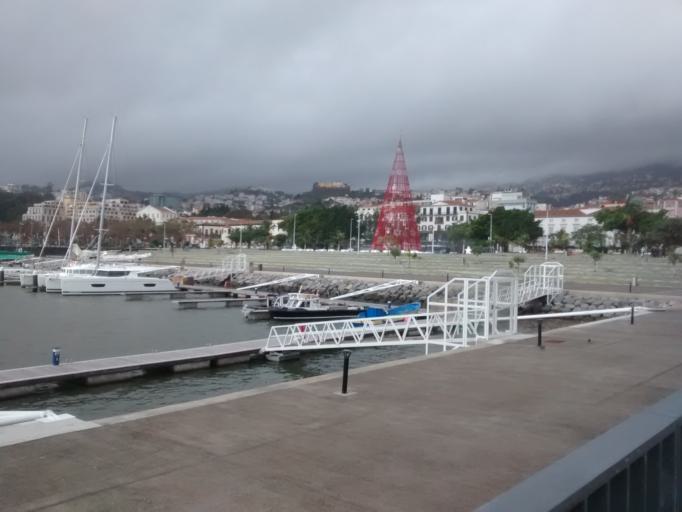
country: PT
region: Madeira
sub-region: Funchal
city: Funchal
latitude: 32.6456
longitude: -16.9066
